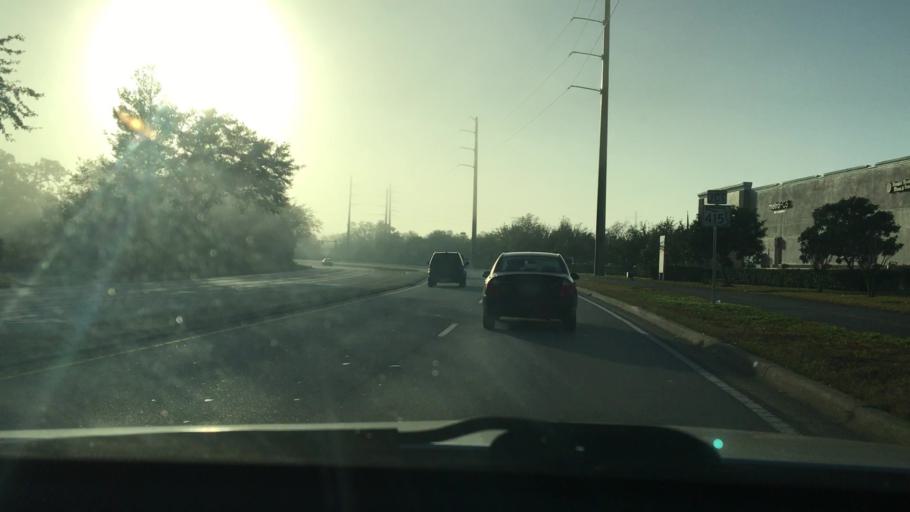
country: US
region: Florida
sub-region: Volusia County
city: Deltona
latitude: 28.8729
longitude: -81.1646
